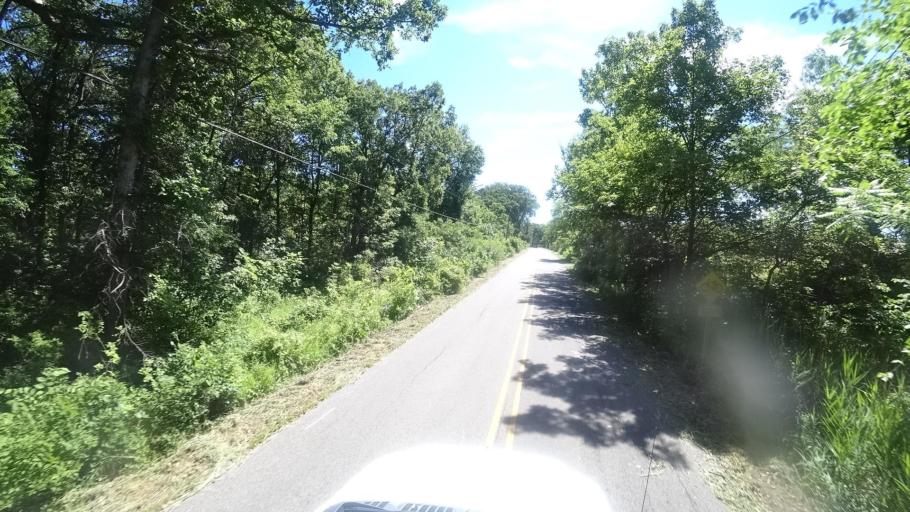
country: US
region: Indiana
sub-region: Porter County
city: Porter
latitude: 41.6297
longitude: -87.0899
